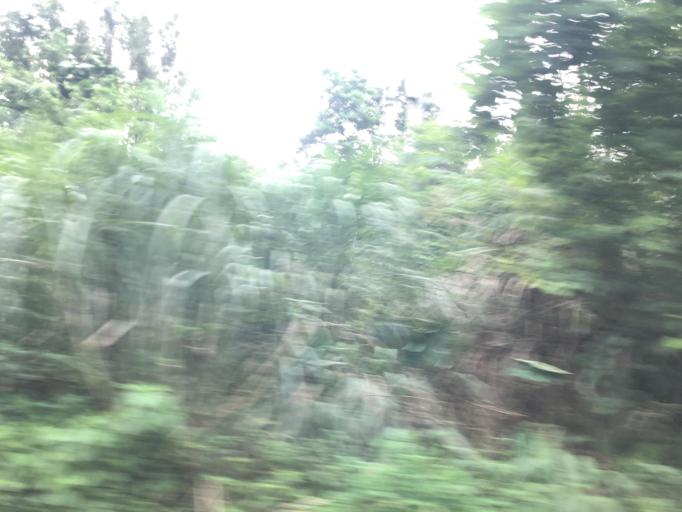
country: TW
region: Taiwan
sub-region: Keelung
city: Keelung
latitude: 25.1592
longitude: 121.6477
